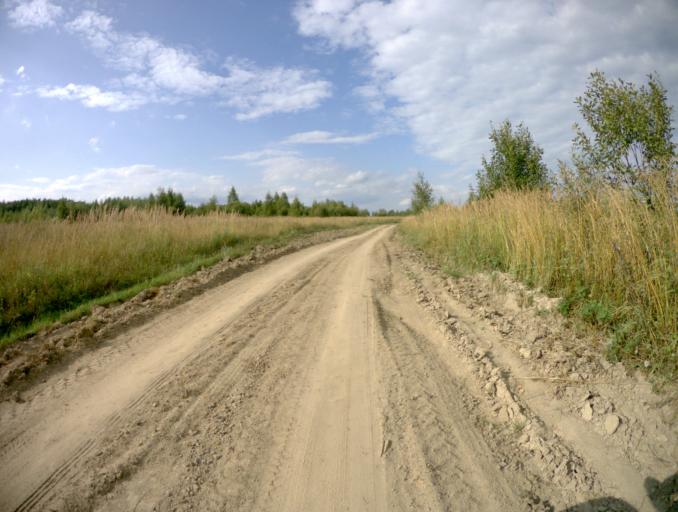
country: RU
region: Vladimir
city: Raduzhnyy
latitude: 55.9829
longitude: 40.3774
